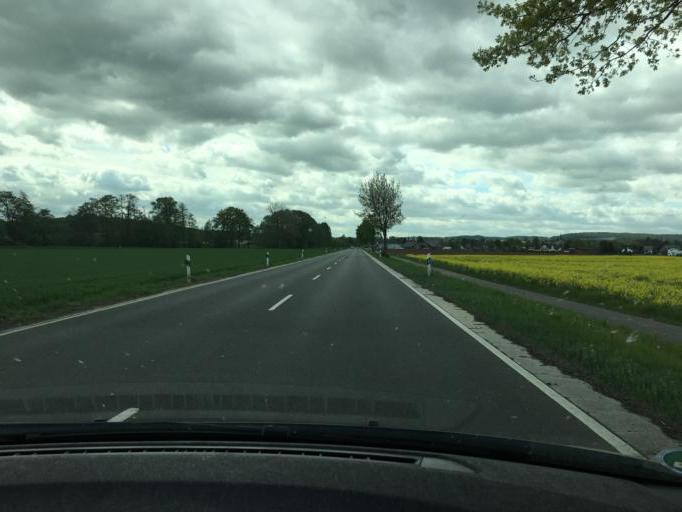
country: DE
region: North Rhine-Westphalia
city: Zulpich
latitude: 50.6550
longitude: 6.6474
